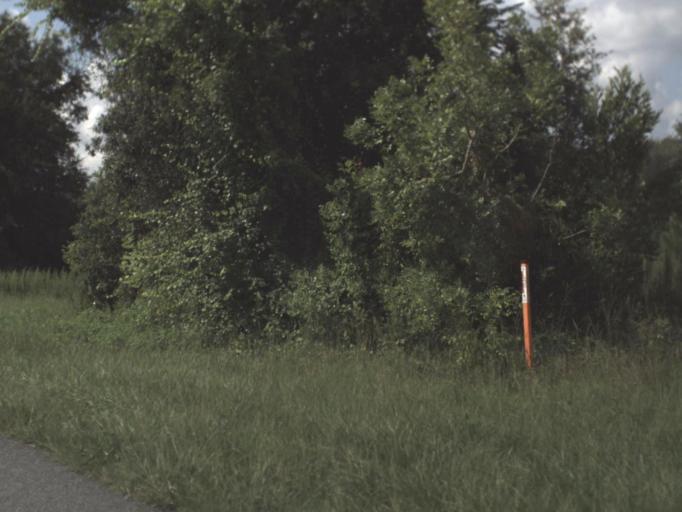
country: US
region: Florida
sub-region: Citrus County
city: Citrus Springs
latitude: 28.9736
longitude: -82.4237
